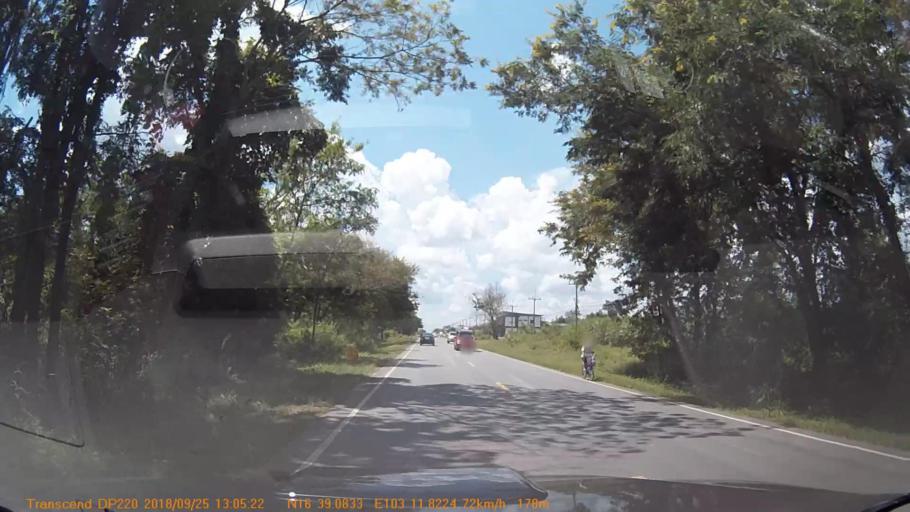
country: TH
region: Kalasin
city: Huai Mek
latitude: 16.6514
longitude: 103.1970
